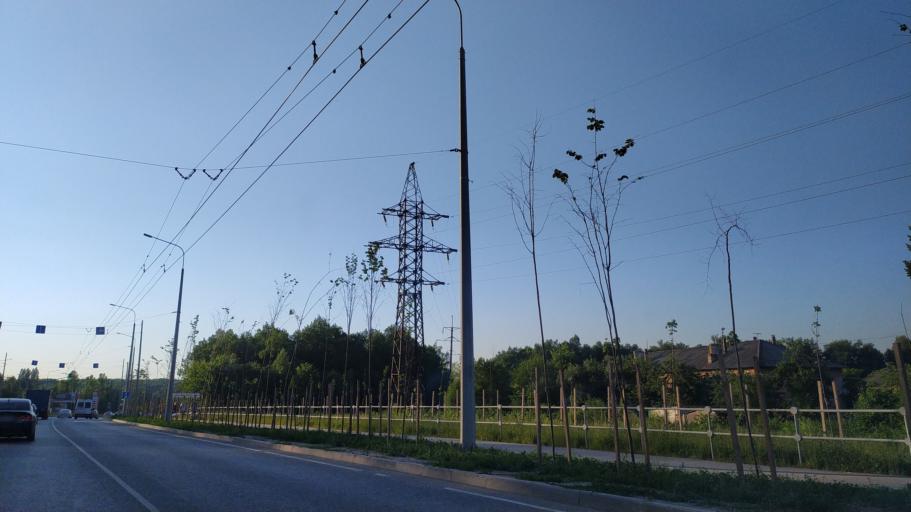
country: RU
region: Chuvashia
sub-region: Cheboksarskiy Rayon
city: Cheboksary
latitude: 56.0803
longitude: 47.2695
